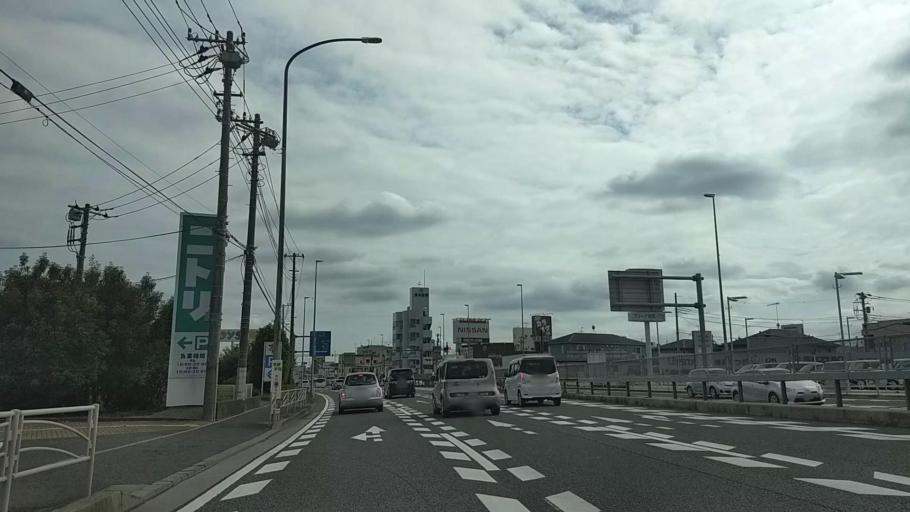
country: JP
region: Kanagawa
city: Atsugi
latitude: 35.4622
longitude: 139.3600
